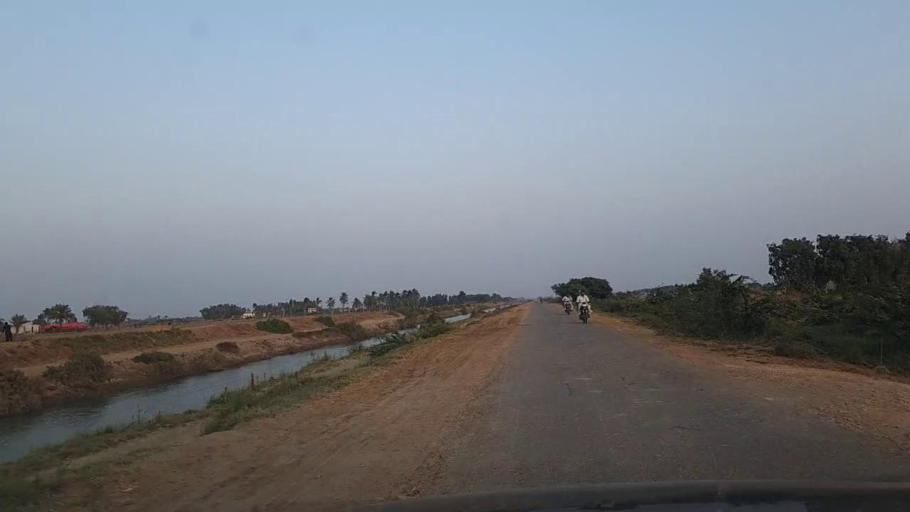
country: PK
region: Sindh
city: Mirpur Sakro
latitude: 24.6374
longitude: 67.5954
